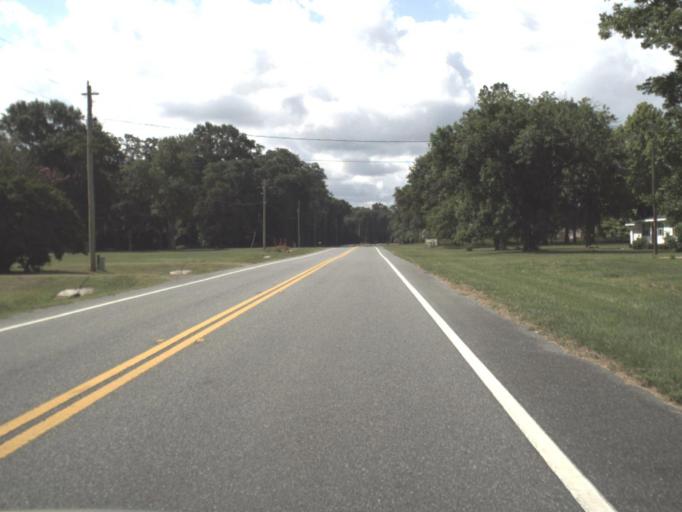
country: US
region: Florida
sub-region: Baker County
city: Macclenny
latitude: 30.3461
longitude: -82.1269
